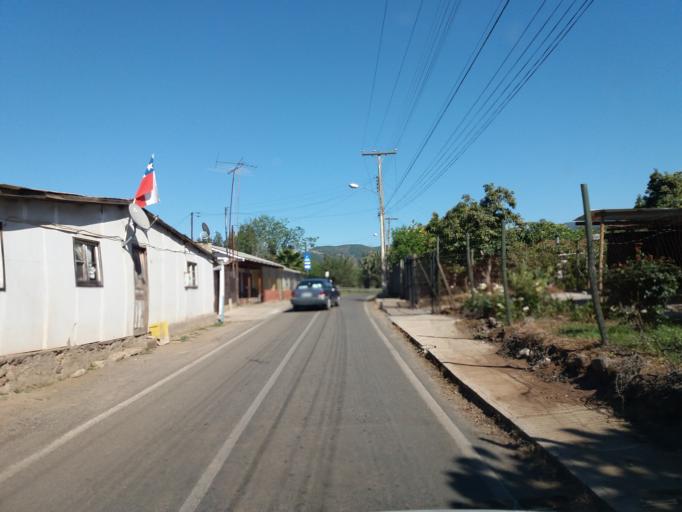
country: CL
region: Valparaiso
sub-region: Provincia de Quillota
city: Quillota
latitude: -32.8648
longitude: -71.2711
